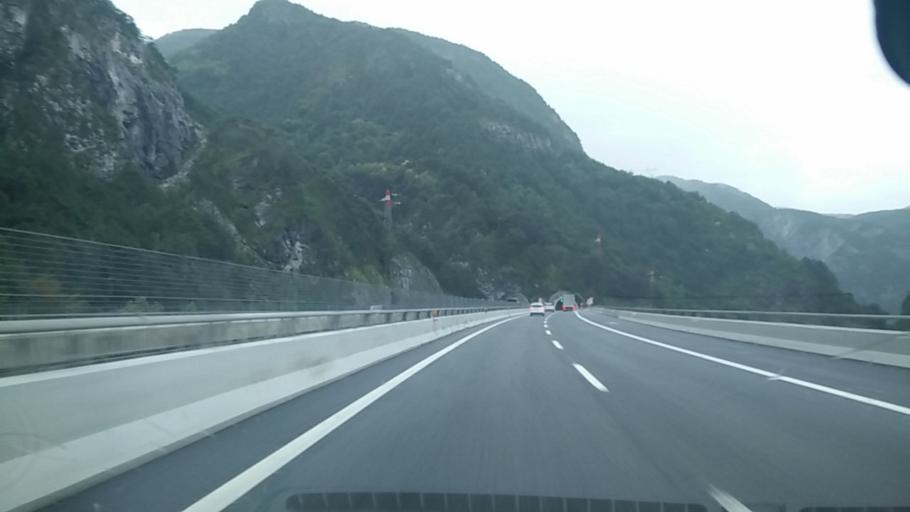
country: IT
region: Friuli Venezia Giulia
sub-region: Provincia di Udine
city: Chiusaforte
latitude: 46.4224
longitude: 13.3196
